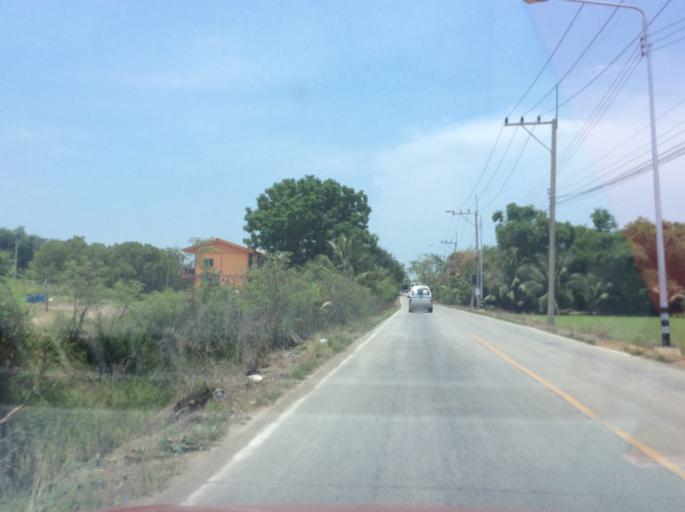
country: TH
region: Pathum Thani
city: Ban Lam Luk Ka
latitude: 13.9859
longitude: 100.7735
